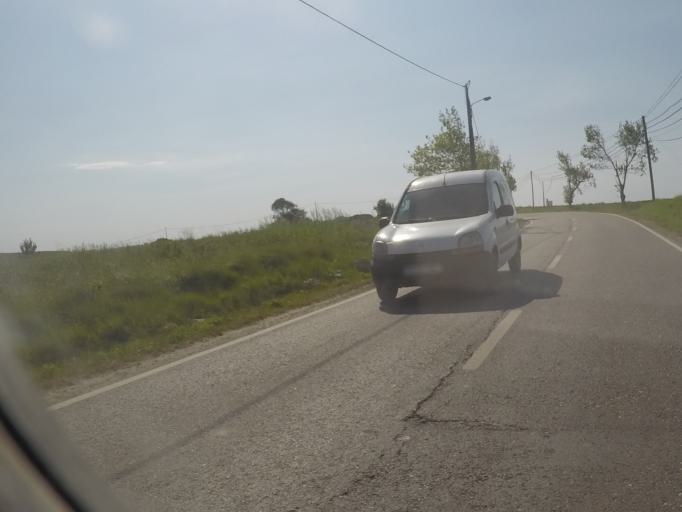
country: PT
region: Setubal
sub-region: Sesimbra
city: Sesimbra
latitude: 38.4461
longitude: -9.1536
